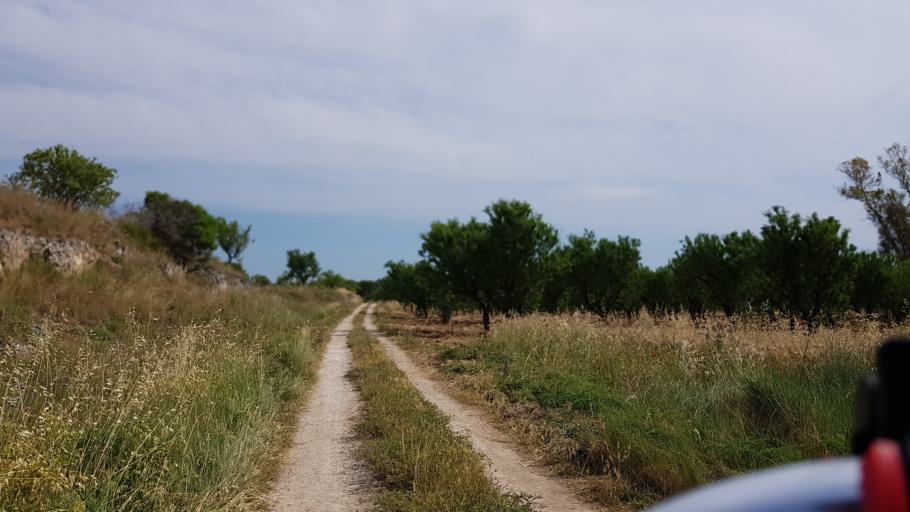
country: IT
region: Apulia
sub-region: Provincia di Brindisi
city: San Vito dei Normanni
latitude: 40.6615
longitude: 17.7991
